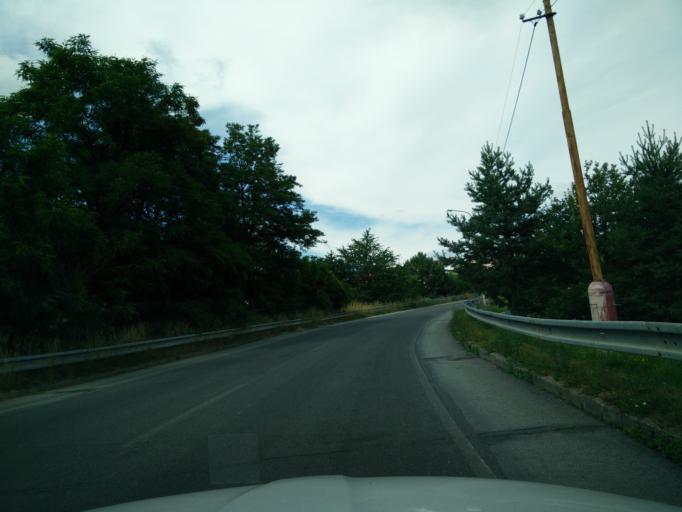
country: SK
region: Nitriansky
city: Bojnice
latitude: 48.8154
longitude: 18.5821
